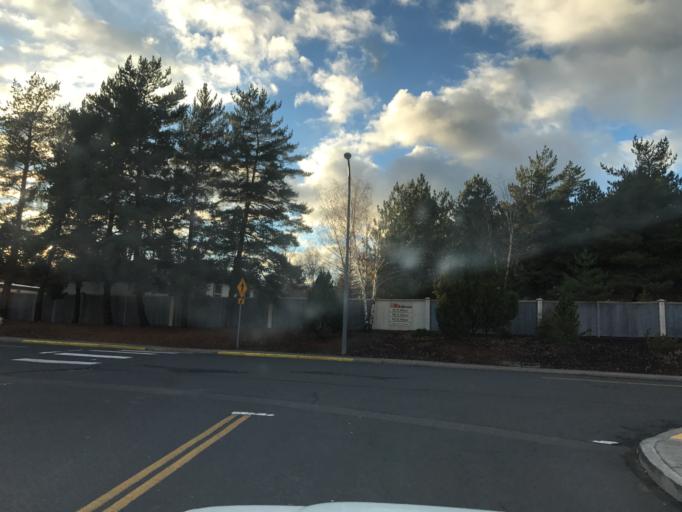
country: US
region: Idaho
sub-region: Latah County
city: Moscow
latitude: 46.7387
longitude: -117.0038
